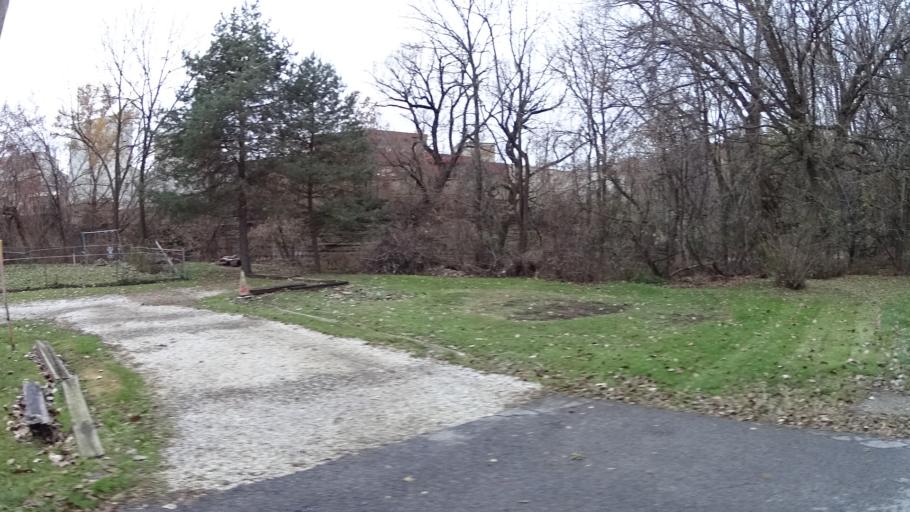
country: US
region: Ohio
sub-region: Lorain County
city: Elyria
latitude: 41.3718
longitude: -82.1003
